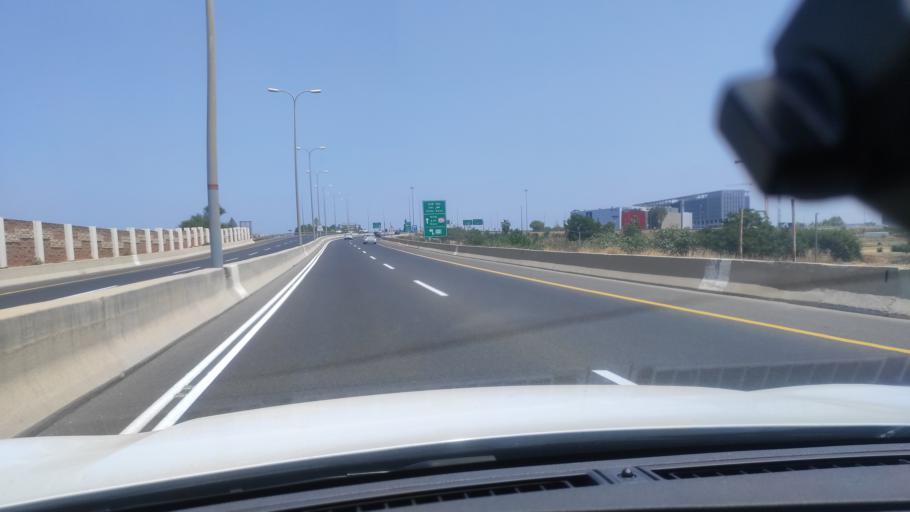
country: IL
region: Central District
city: Kfar Saba
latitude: 32.1601
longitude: 34.9263
